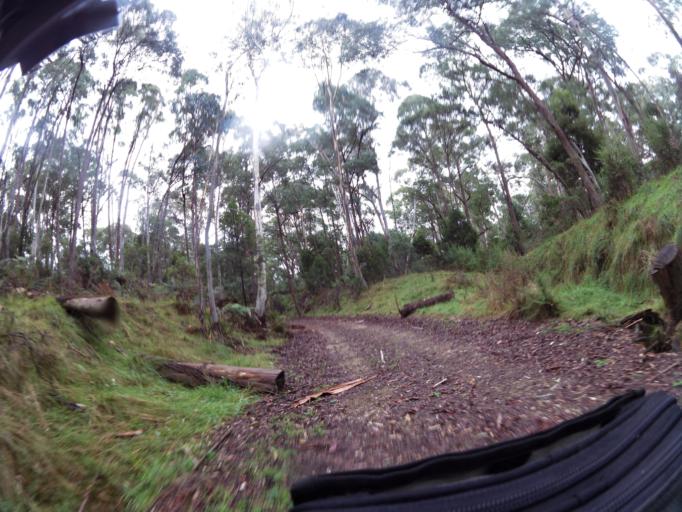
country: AU
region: New South Wales
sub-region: Greater Hume Shire
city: Holbrook
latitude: -36.1467
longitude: 147.4616
